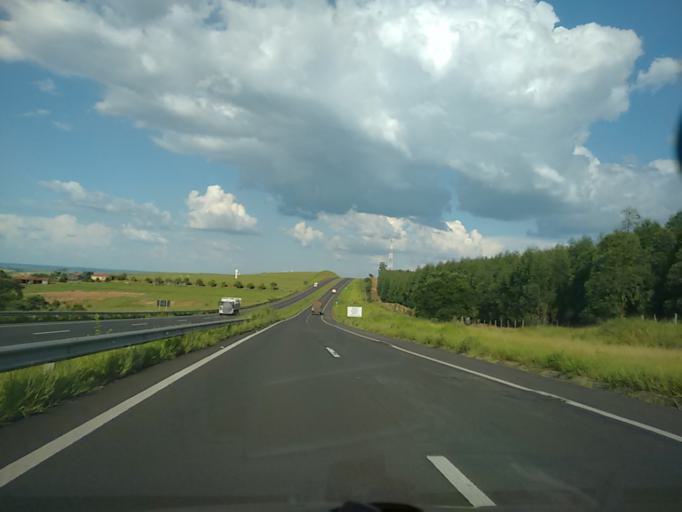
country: BR
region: Sao Paulo
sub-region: Duartina
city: Duartina
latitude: -22.3251
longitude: -49.4259
